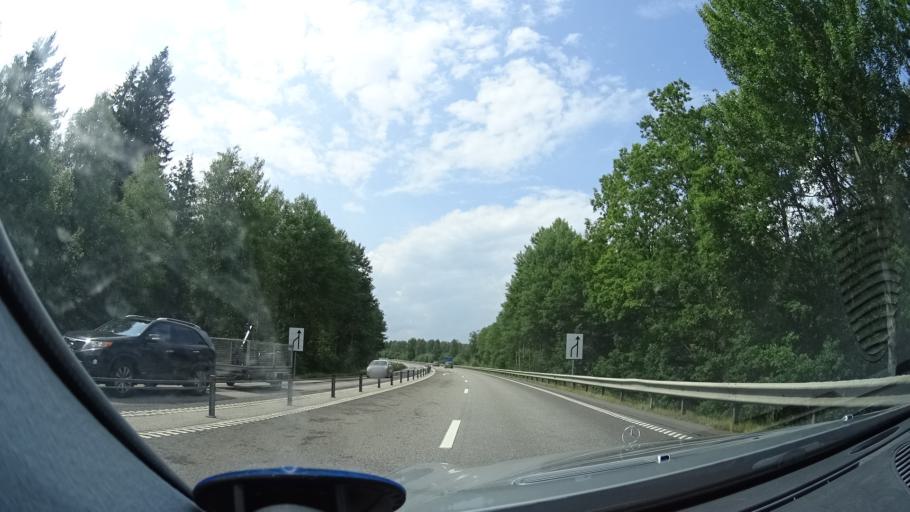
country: SE
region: Kalmar
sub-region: Nybro Kommun
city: Nybro
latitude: 56.7340
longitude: 15.8728
